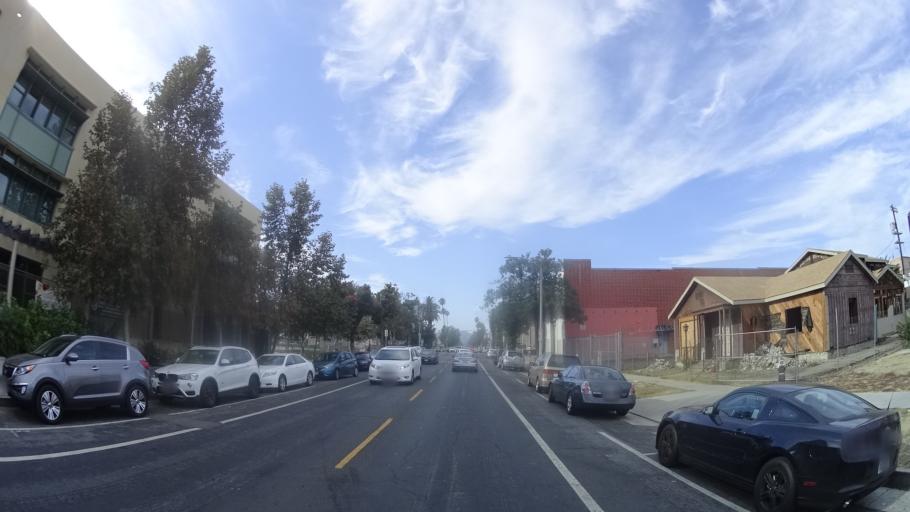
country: US
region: California
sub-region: Los Angeles County
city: Hollywood
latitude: 34.0702
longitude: -118.3079
